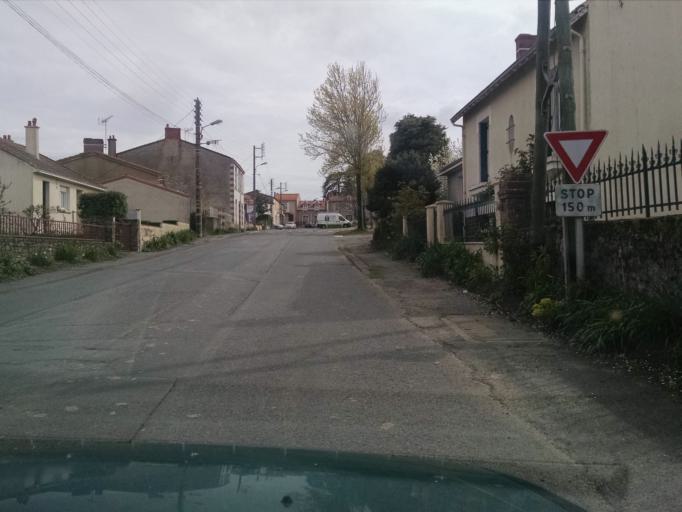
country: FR
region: Pays de la Loire
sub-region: Departement de la Loire-Atlantique
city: Gorges
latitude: 47.1025
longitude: -1.3043
